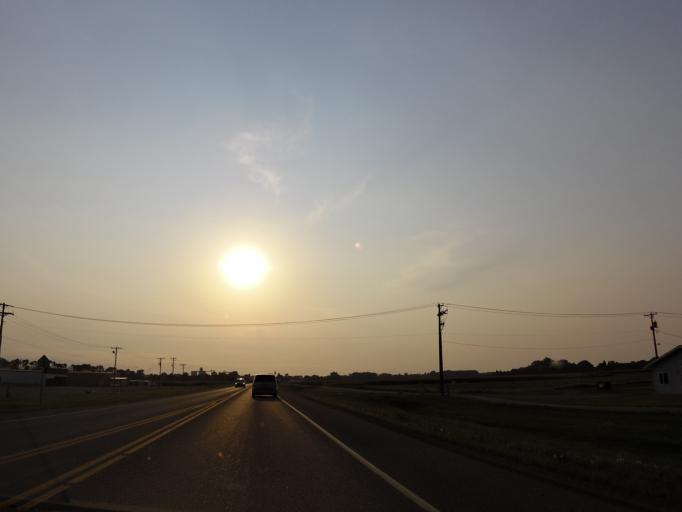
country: US
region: North Dakota
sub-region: Traill County
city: Mayville
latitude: 47.4985
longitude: -97.3509
